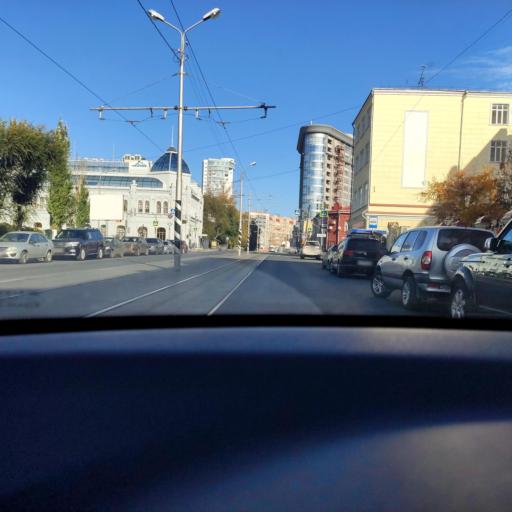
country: RU
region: Samara
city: Samara
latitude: 53.1964
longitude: 50.1053
